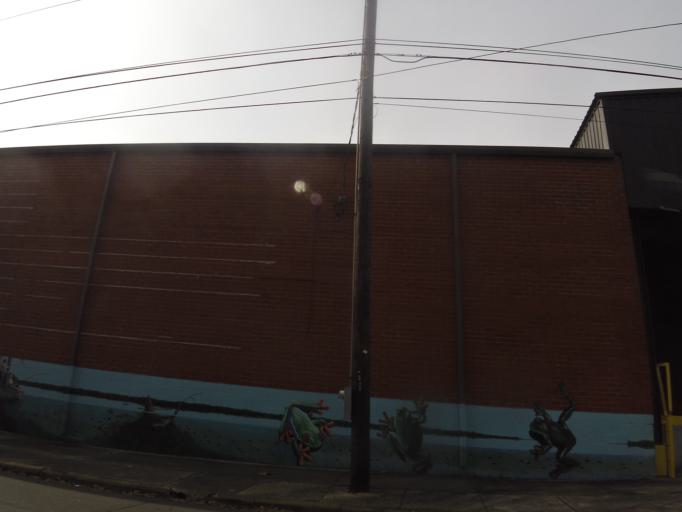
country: US
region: Alabama
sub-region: Houston County
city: Dothan
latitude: 31.2284
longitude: -85.3918
